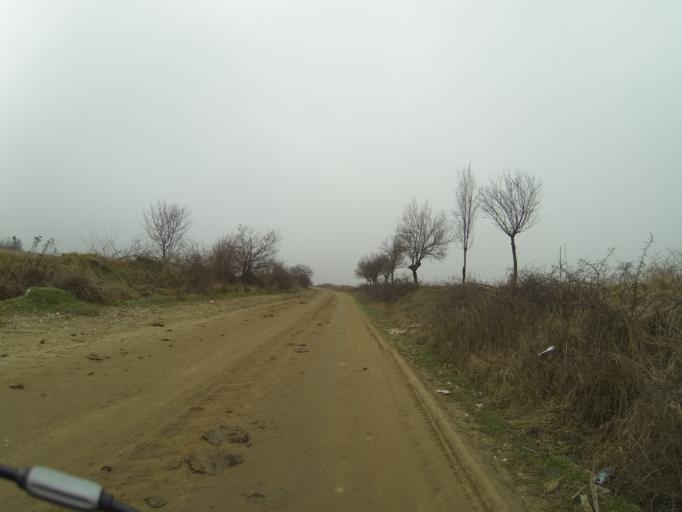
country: RO
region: Mehedinti
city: Dumbrava de Sus
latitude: 44.4825
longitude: 23.0615
